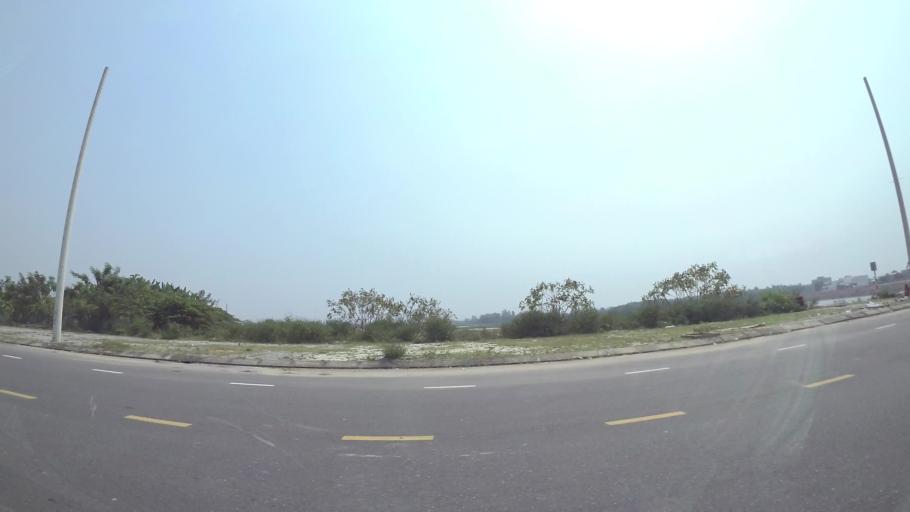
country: VN
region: Da Nang
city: Cam Le
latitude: 15.9850
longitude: 108.2168
